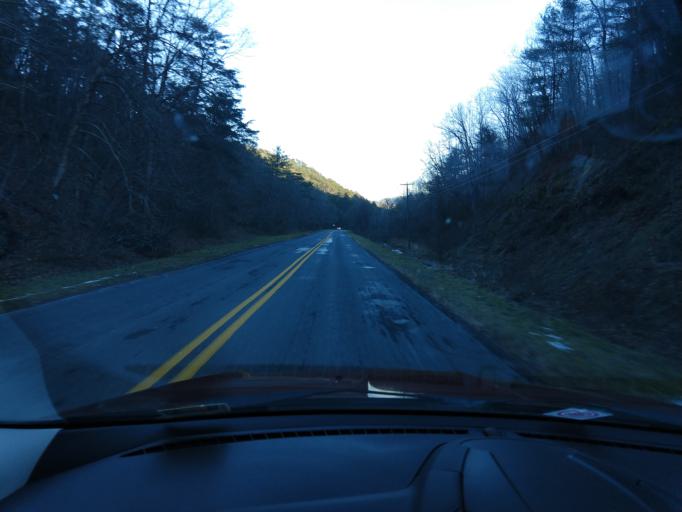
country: US
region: Virginia
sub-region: Alleghany County
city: Clifton Forge
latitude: 37.8295
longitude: -79.8374
